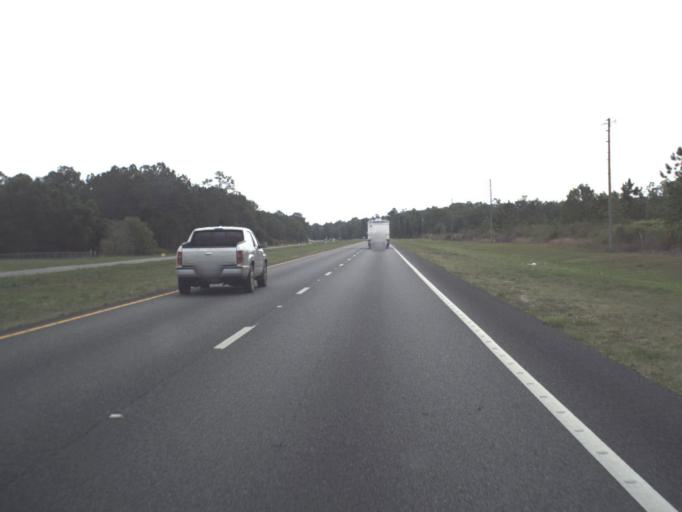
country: US
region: Florida
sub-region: Sumter County
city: Wildwood
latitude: 28.8575
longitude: -82.0719
